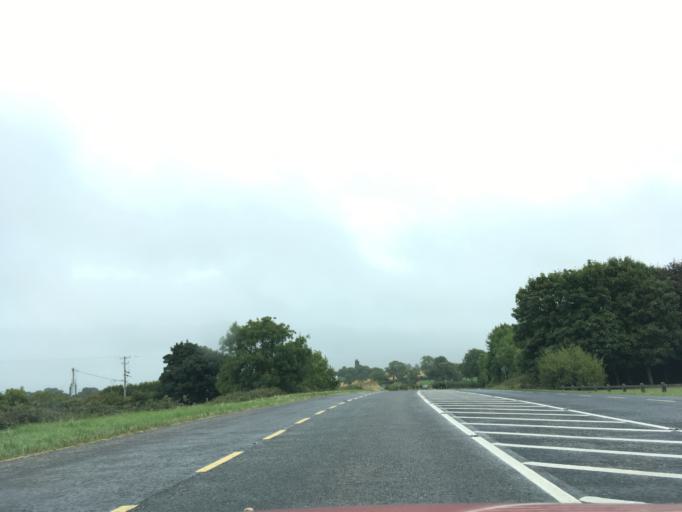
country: IE
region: Munster
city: Carrick-on-Suir
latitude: 52.3656
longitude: -7.5168
